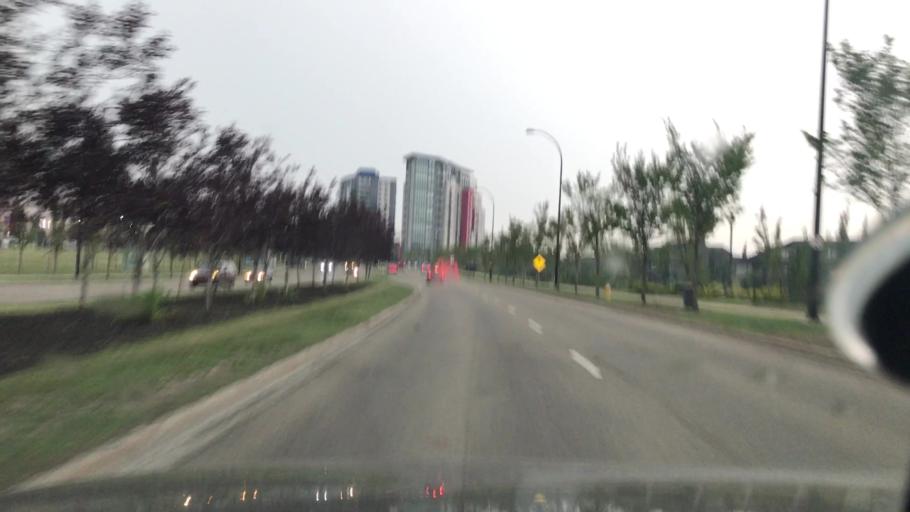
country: CA
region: Alberta
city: Devon
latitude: 53.4348
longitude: -113.6065
